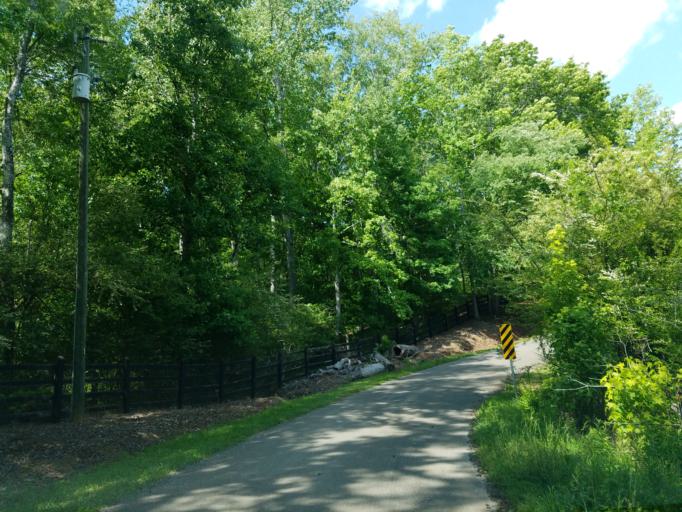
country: US
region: Georgia
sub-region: Cherokee County
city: Ball Ground
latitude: 34.2846
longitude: -84.3115
